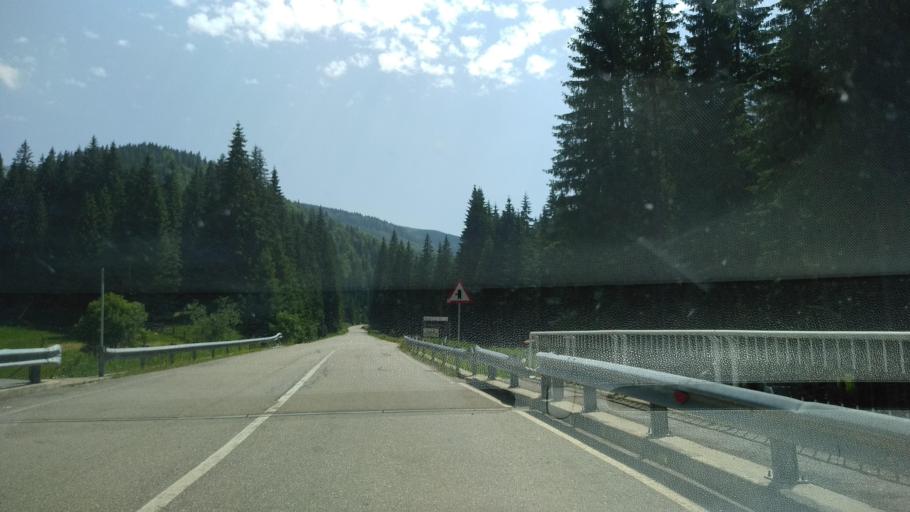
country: RO
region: Gorj
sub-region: Comuna Pades
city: Closani
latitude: 45.2630
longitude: 22.8708
